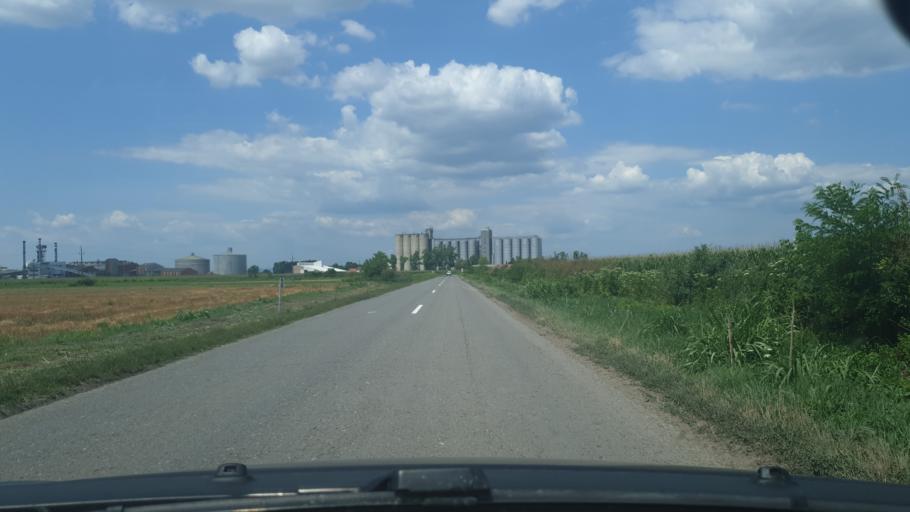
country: RS
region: Autonomna Pokrajina Vojvodina
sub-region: Sremski Okrug
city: Pecinci
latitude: 44.8793
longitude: 19.9609
